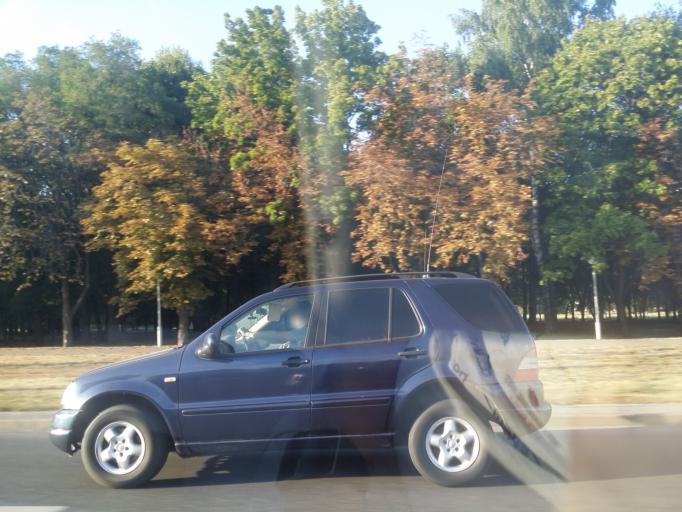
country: BY
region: Minsk
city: Minsk
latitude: 53.8782
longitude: 27.6123
